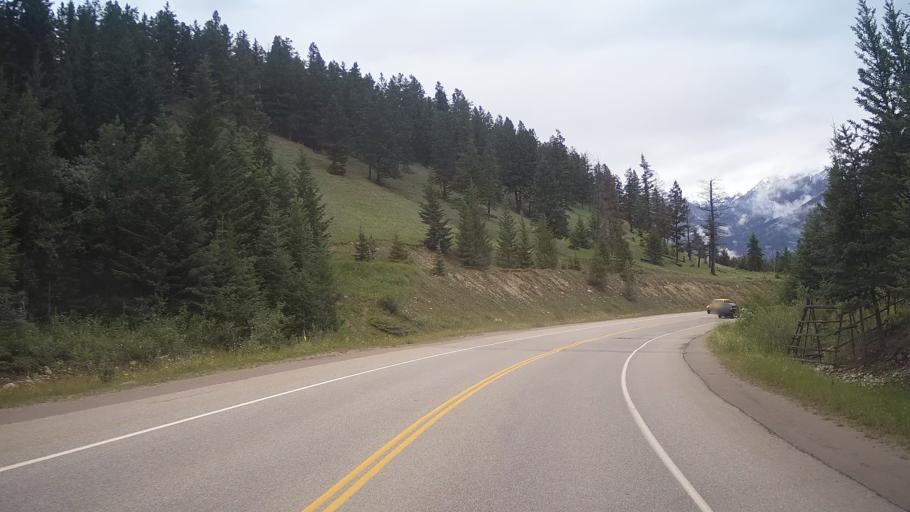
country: CA
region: Alberta
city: Jasper Park Lodge
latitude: 52.8933
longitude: -118.0755
